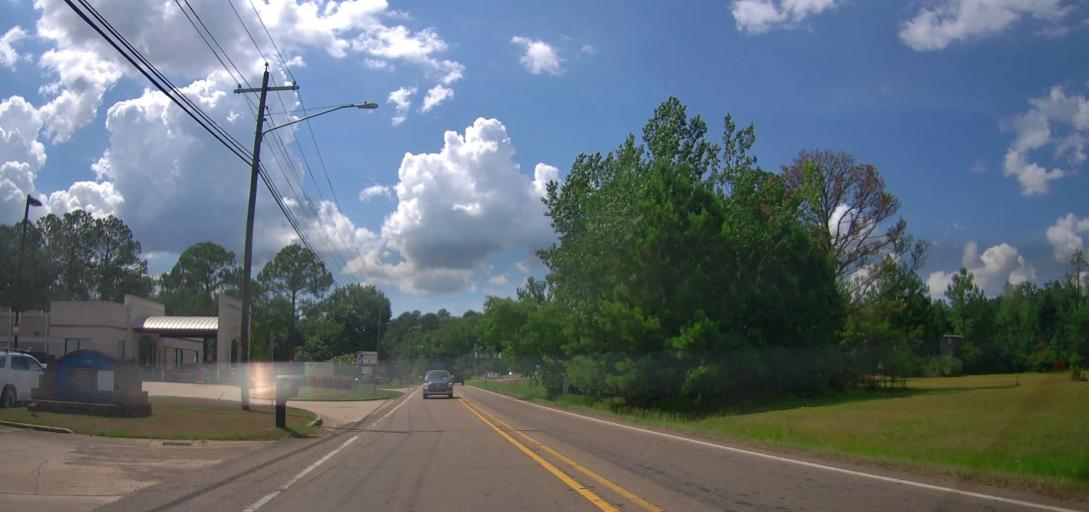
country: US
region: Mississippi
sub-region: Lowndes County
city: Columbus
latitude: 33.5367
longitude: -88.4310
